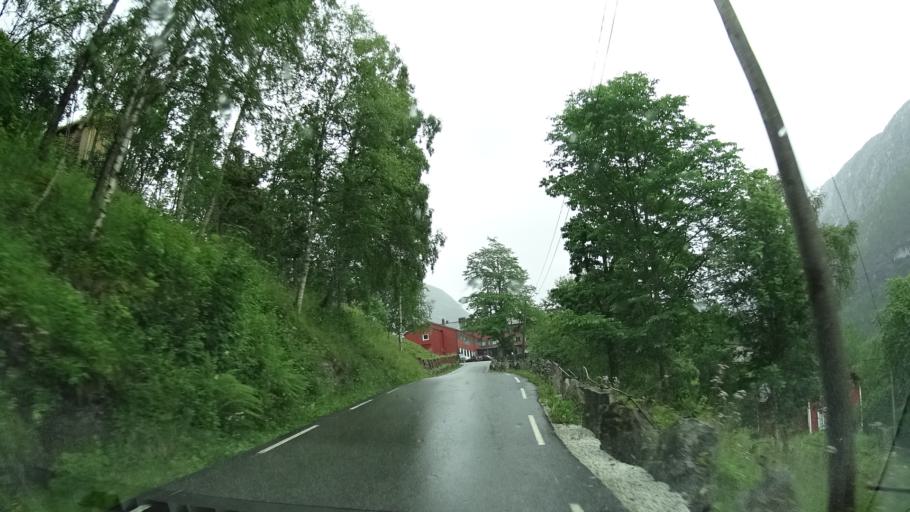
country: NO
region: Sogn og Fjordane
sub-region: Vik
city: Vik
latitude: 60.8341
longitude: 6.6793
